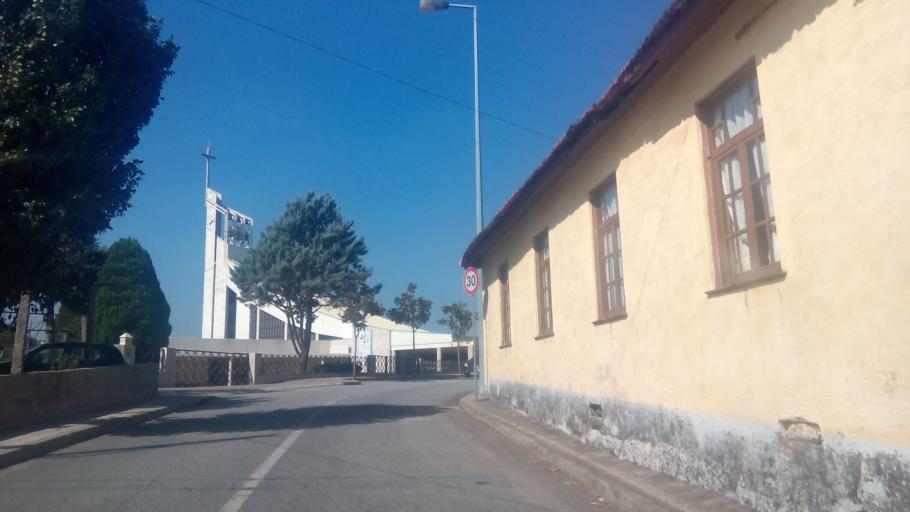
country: PT
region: Porto
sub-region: Paredes
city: Madalena
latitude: 41.2161
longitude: -8.3354
